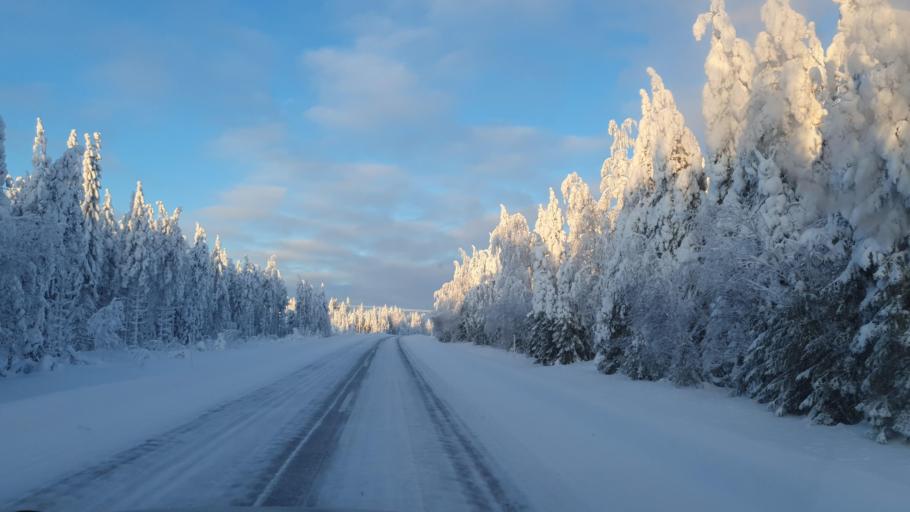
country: FI
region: Kainuu
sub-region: Kajaani
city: Vuokatti
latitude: 64.2418
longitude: 28.2325
